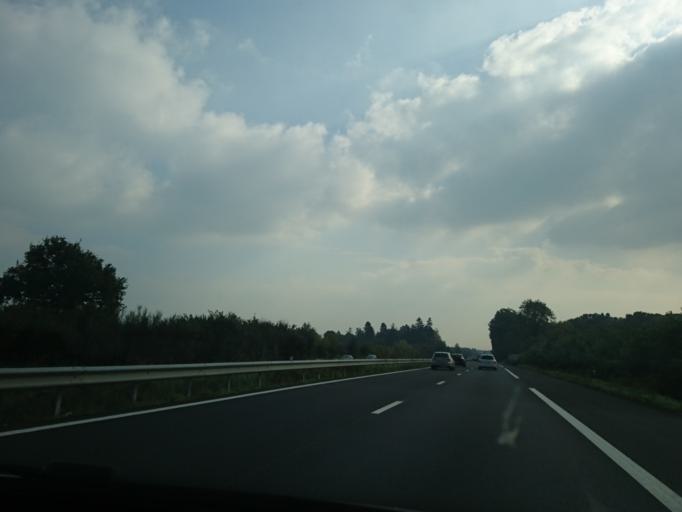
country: FR
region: Pays de la Loire
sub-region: Departement de la Loire-Atlantique
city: La Grigonnais
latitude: 47.5057
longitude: -1.6392
